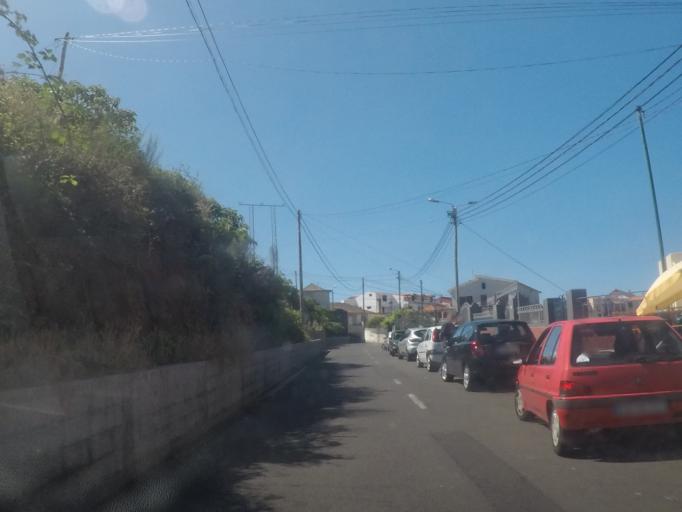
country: PT
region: Madeira
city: Camara de Lobos
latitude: 32.6709
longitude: -16.9677
